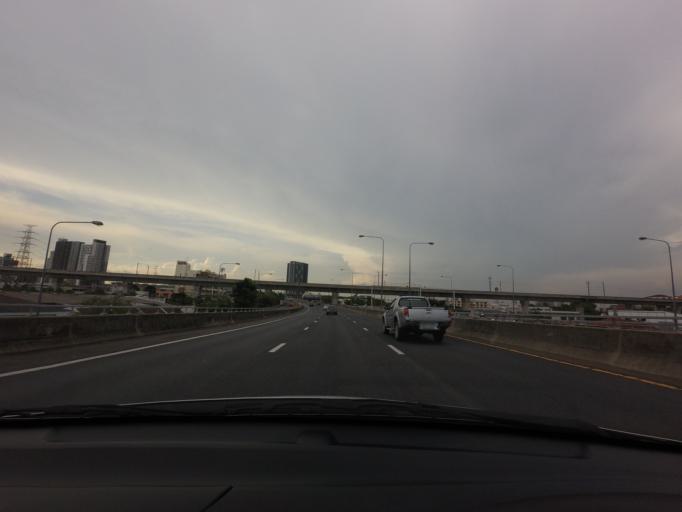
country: TH
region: Bangkok
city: Watthana
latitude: 13.7411
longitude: 100.6050
